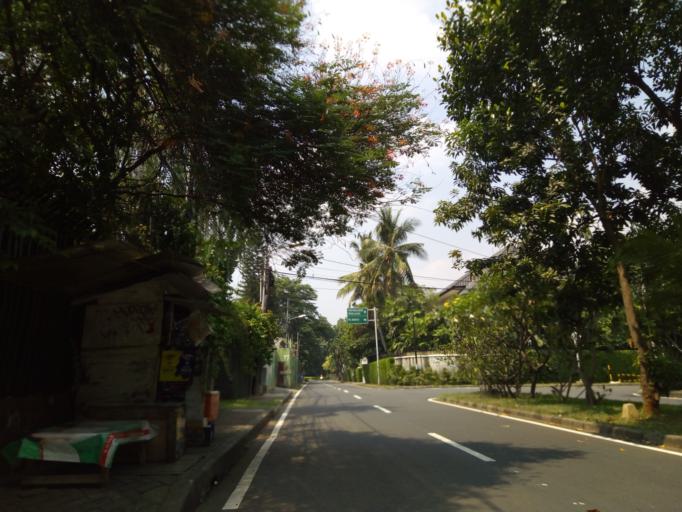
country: ID
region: Jakarta Raya
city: Jakarta
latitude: -6.2025
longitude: 106.8401
